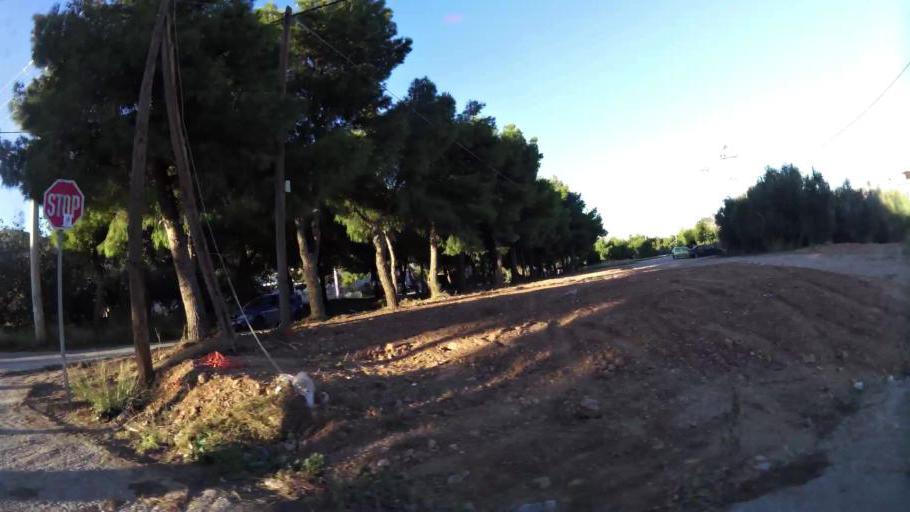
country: GR
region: Attica
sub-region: Nomarchia Anatolikis Attikis
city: Acharnes
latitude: 38.1015
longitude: 23.7201
